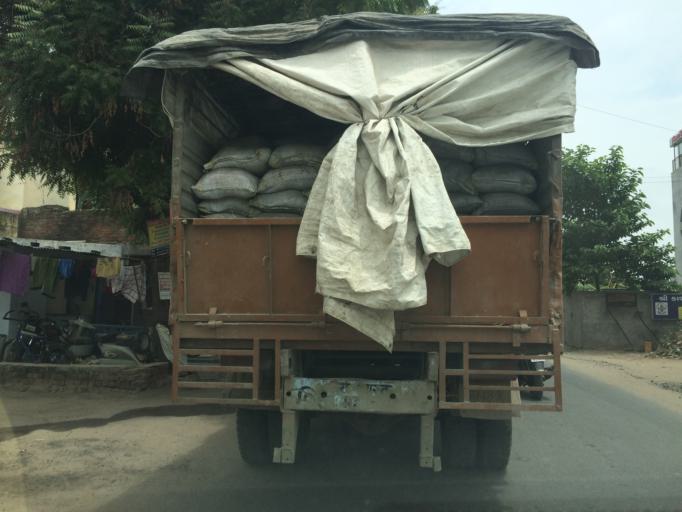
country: IN
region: Gujarat
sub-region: Ahmadabad
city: Ahmedabad
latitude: 23.0826
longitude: 72.5662
